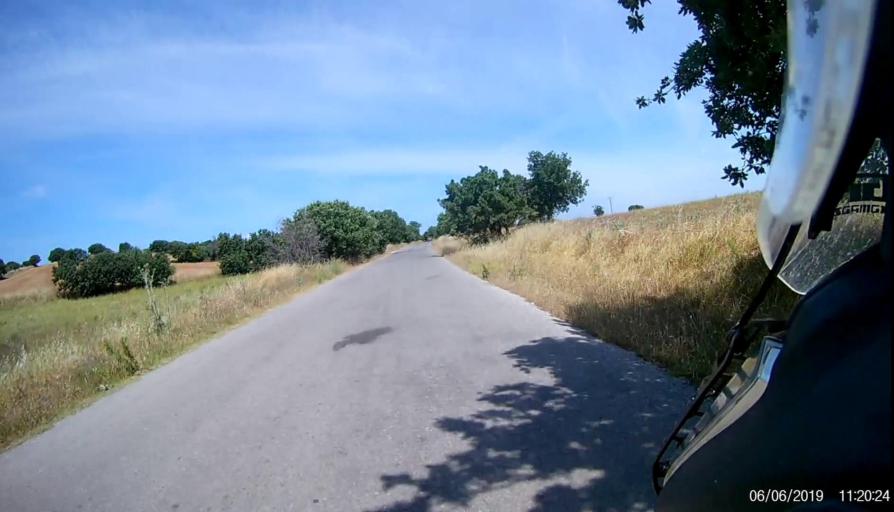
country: TR
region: Canakkale
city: Gulpinar
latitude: 39.6660
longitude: 26.1636
